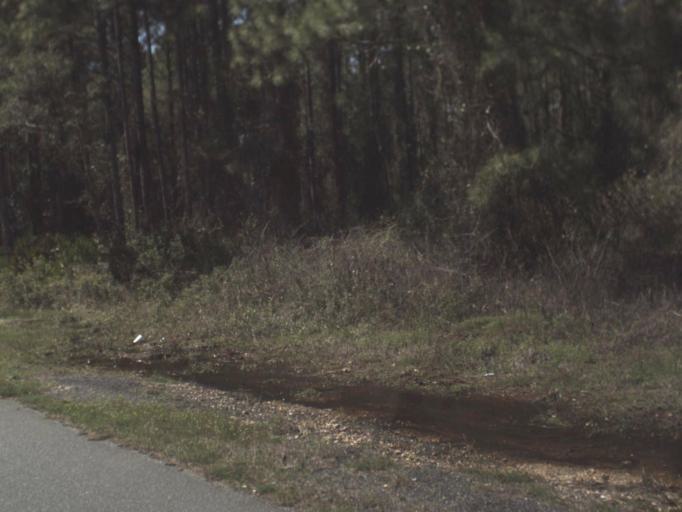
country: US
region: Florida
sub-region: Franklin County
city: Carrabelle
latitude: 29.9142
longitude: -84.5258
